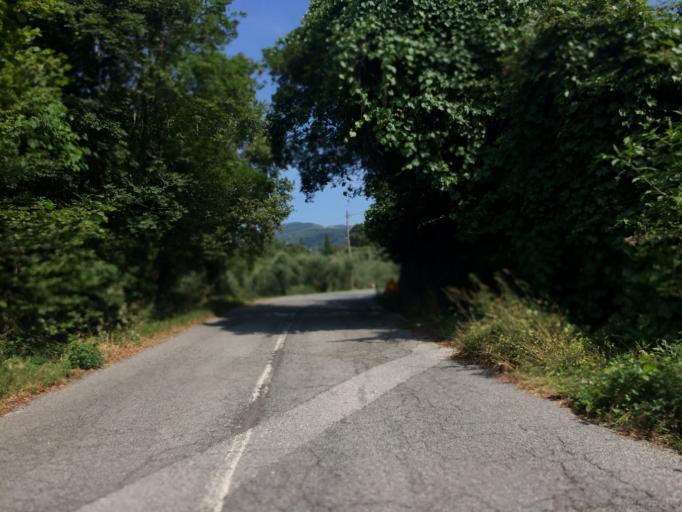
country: IT
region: Liguria
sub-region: Provincia di Savona
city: Varazze
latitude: 44.3830
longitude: 8.5699
